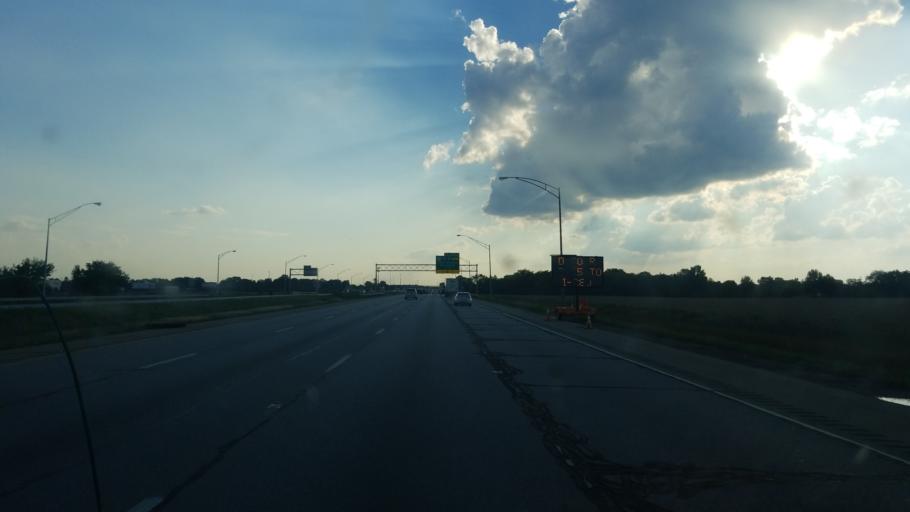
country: US
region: Ohio
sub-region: Wood County
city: Rossford
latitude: 41.5814
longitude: -83.5683
